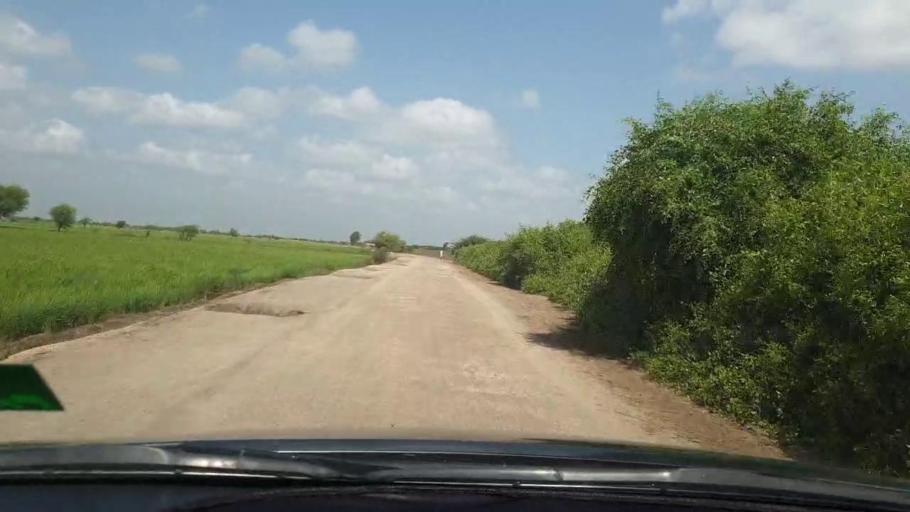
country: PK
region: Sindh
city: Tando Bago
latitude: 24.8612
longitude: 69.0581
